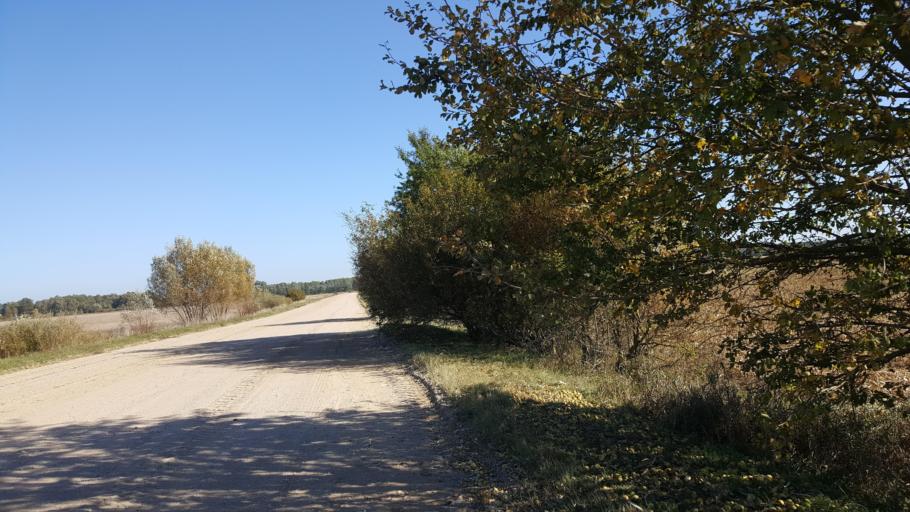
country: BY
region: Brest
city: Kamyanyets
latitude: 52.4188
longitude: 23.8643
